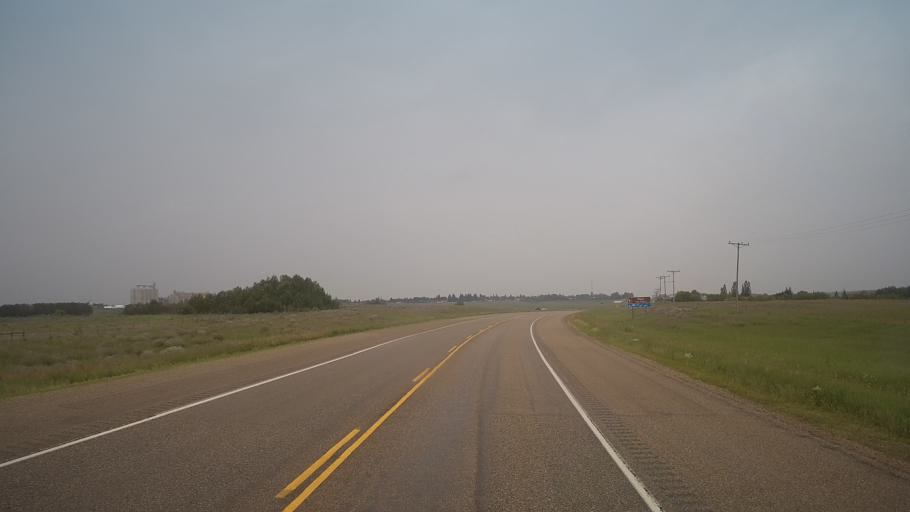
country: CA
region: Saskatchewan
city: Biggar
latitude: 52.0565
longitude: -107.9482
